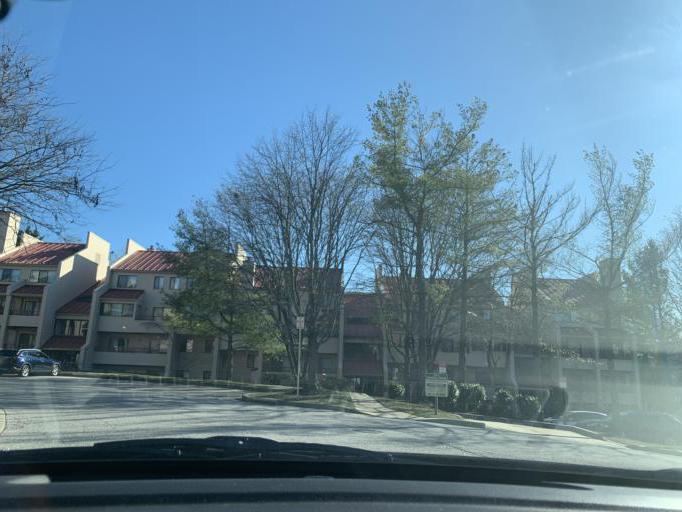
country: US
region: Maryland
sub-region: Baltimore County
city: Garrison
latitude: 39.4015
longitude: -76.7582
